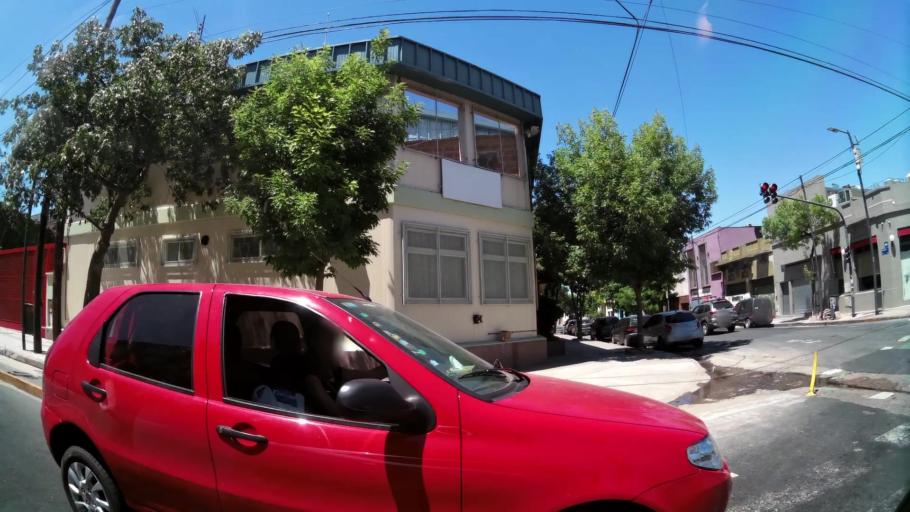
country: AR
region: Buenos Aires F.D.
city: Buenos Aires
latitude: -34.6392
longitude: -58.4032
